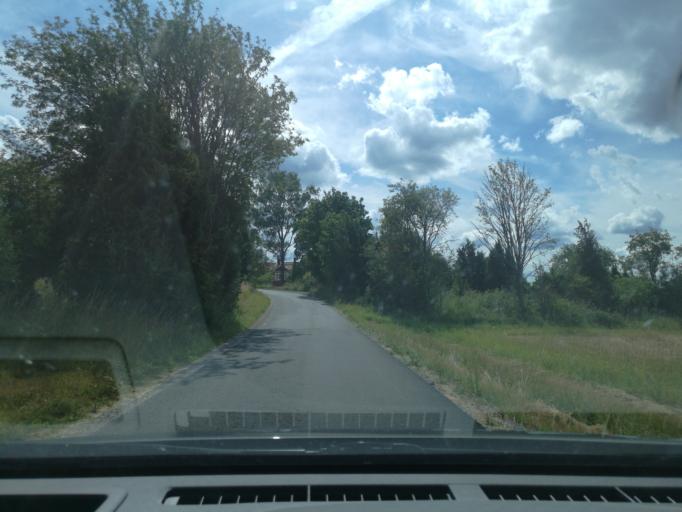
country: SE
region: Stockholm
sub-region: Sigtuna Kommun
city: Marsta
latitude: 59.6494
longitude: 17.8842
